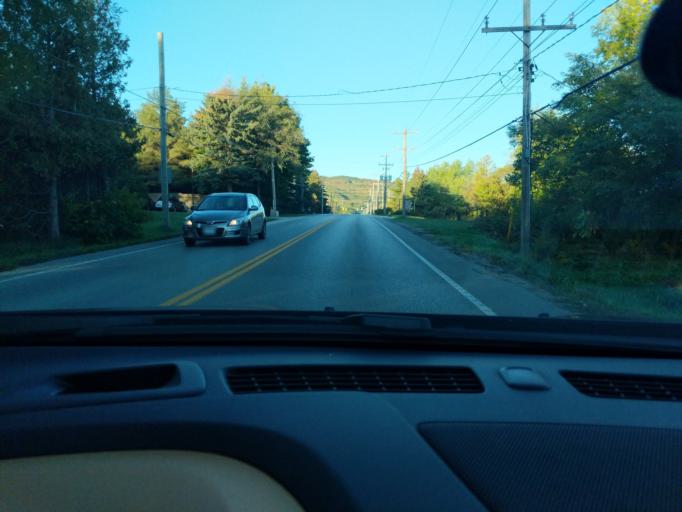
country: CA
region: Ontario
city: Collingwood
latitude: 44.4987
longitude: -80.2820
